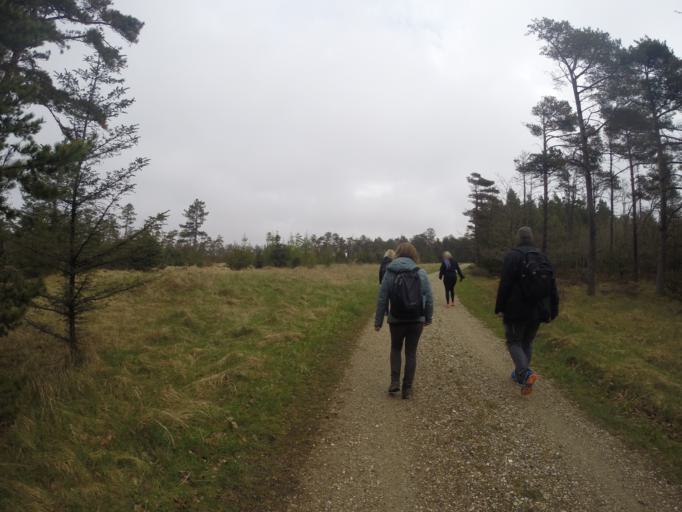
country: DK
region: North Denmark
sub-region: Thisted Kommune
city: Hanstholm
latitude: 57.0374
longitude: 8.5552
